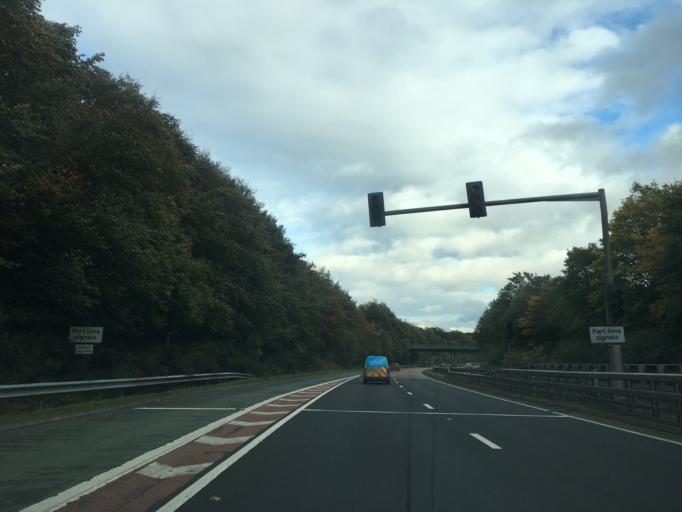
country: GB
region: Scotland
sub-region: Edinburgh
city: Queensferry
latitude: 55.9797
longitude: -3.3509
